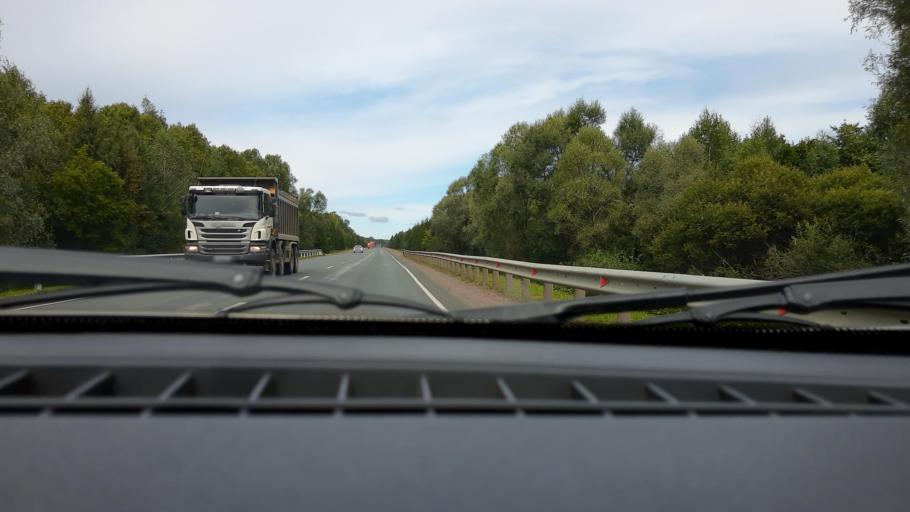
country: RU
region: Bashkortostan
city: Avdon
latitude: 54.8055
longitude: 55.7442
